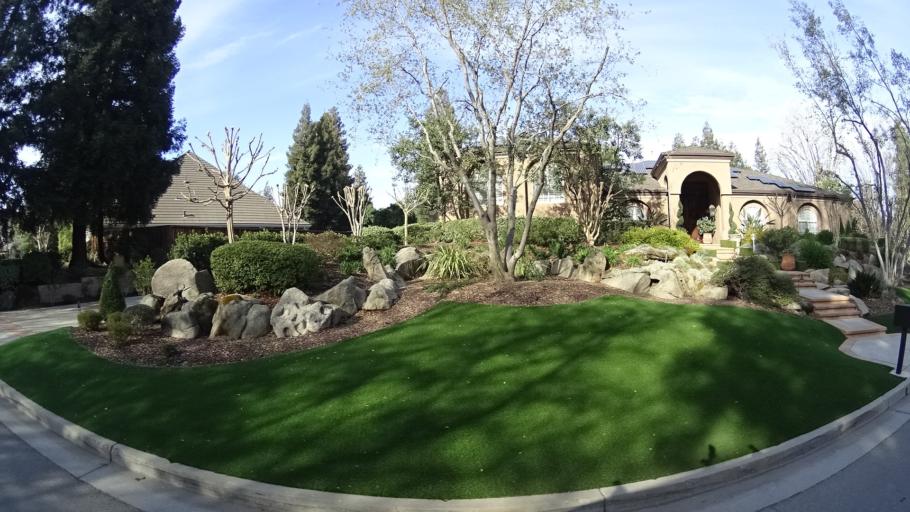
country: US
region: California
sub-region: Fresno County
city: Clovis
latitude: 36.8704
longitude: -119.7741
